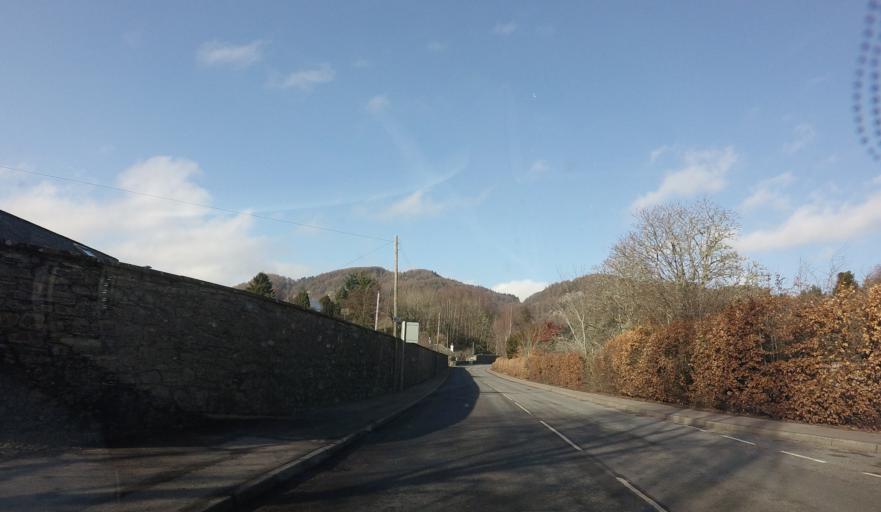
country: GB
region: Scotland
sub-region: Perth and Kinross
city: Bankfoot
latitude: 56.5683
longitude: -3.5871
